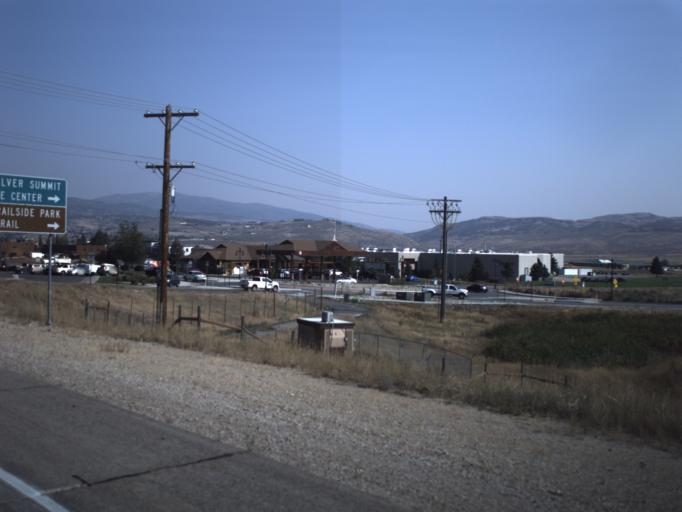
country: US
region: Utah
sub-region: Summit County
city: Snyderville
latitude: 40.7183
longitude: -111.4855
